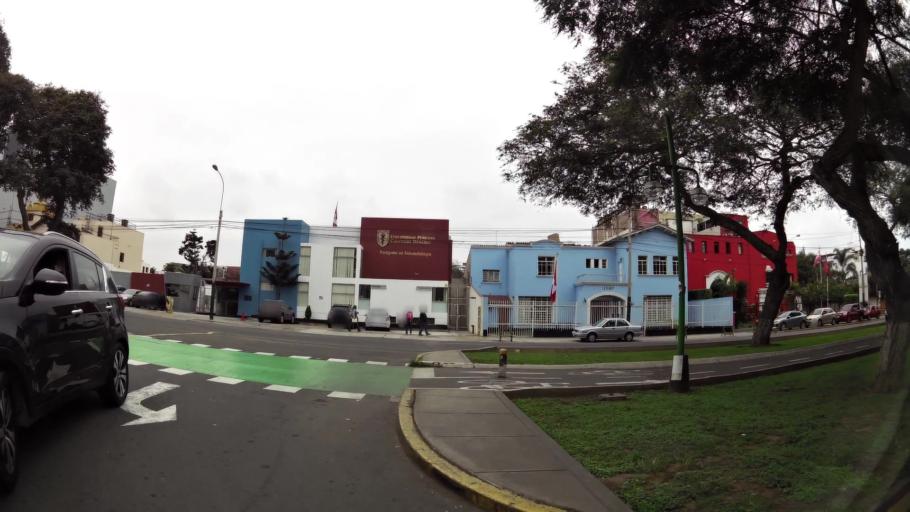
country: PE
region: Lima
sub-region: Lima
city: San Isidro
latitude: -12.0911
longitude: -77.0524
